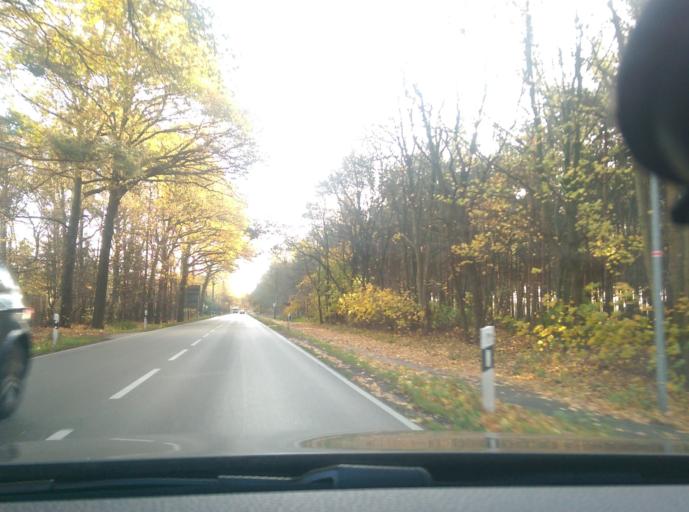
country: DE
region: Lower Saxony
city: Essel
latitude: 52.6726
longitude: 9.6988
